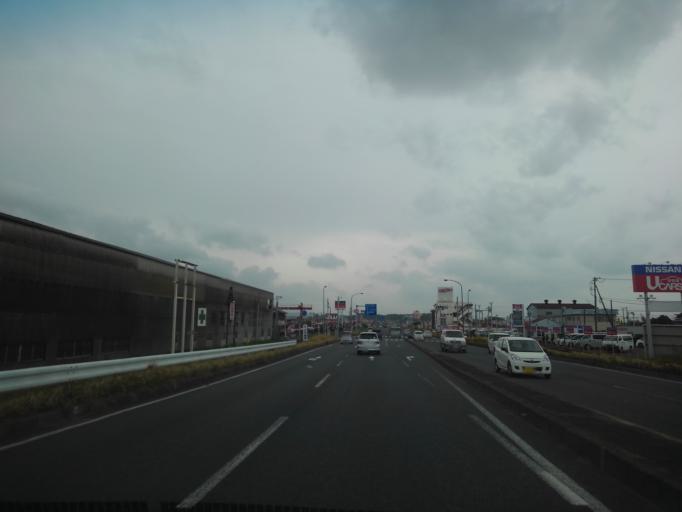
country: JP
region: Chiba
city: Kisarazu
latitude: 35.3988
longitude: 139.9416
